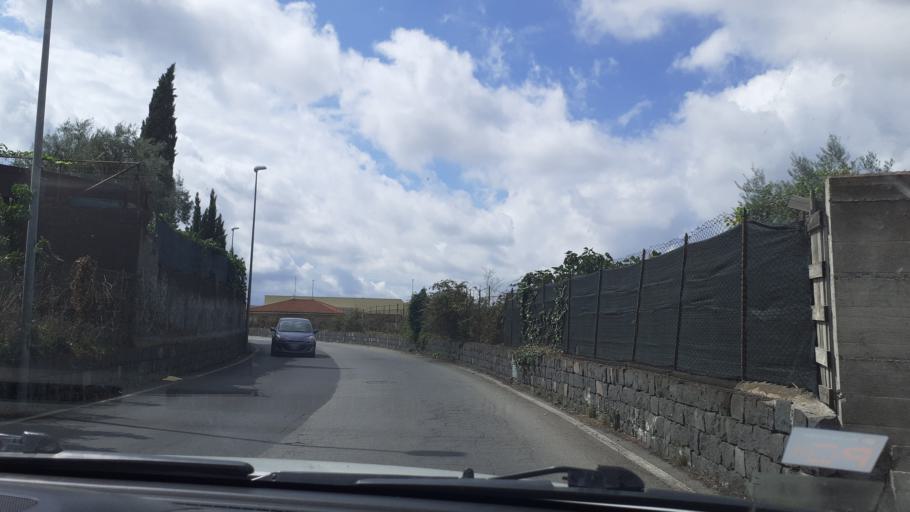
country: IT
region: Sicily
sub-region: Catania
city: San Giovanni la Punta
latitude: 37.5885
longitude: 15.0913
